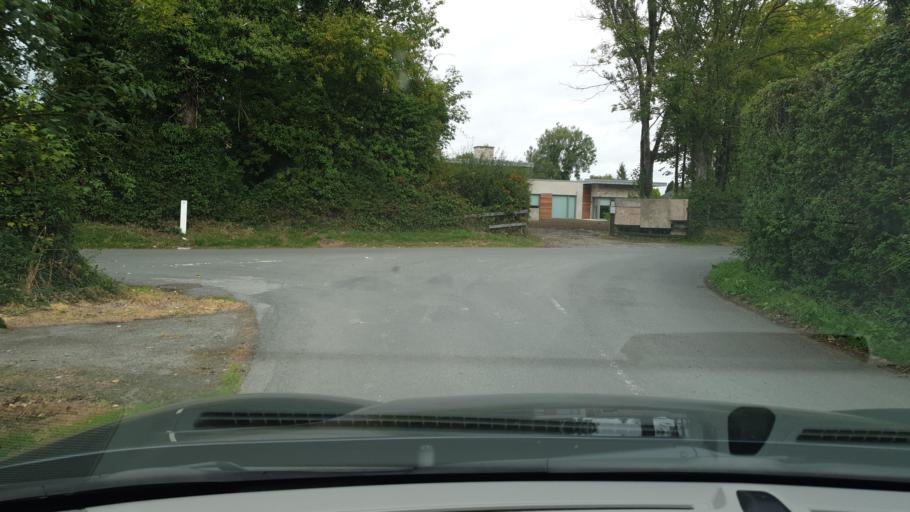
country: IE
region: Leinster
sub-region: Kildare
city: Clane
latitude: 53.2988
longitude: -6.7137
